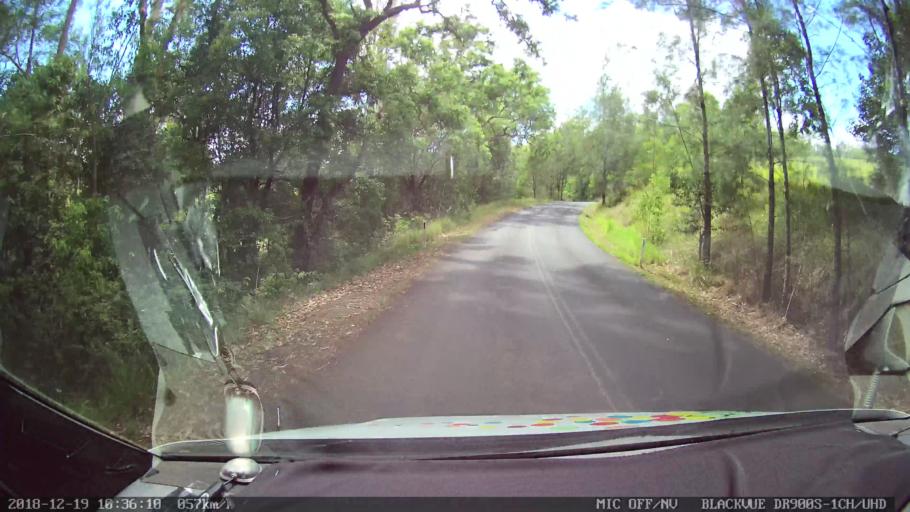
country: AU
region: New South Wales
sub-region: Lismore Municipality
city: Nimbin
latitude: -28.5738
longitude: 153.1421
